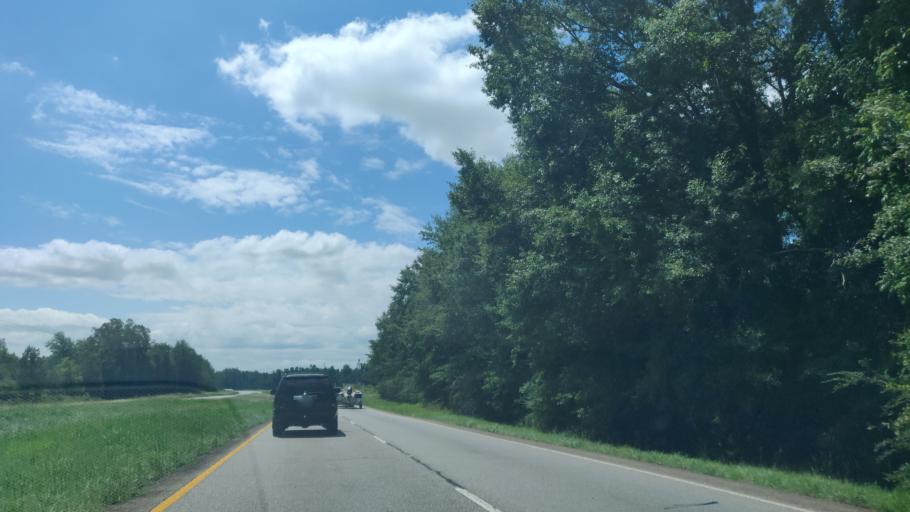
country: US
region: Georgia
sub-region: Stewart County
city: Richland
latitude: 32.0036
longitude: -84.6487
